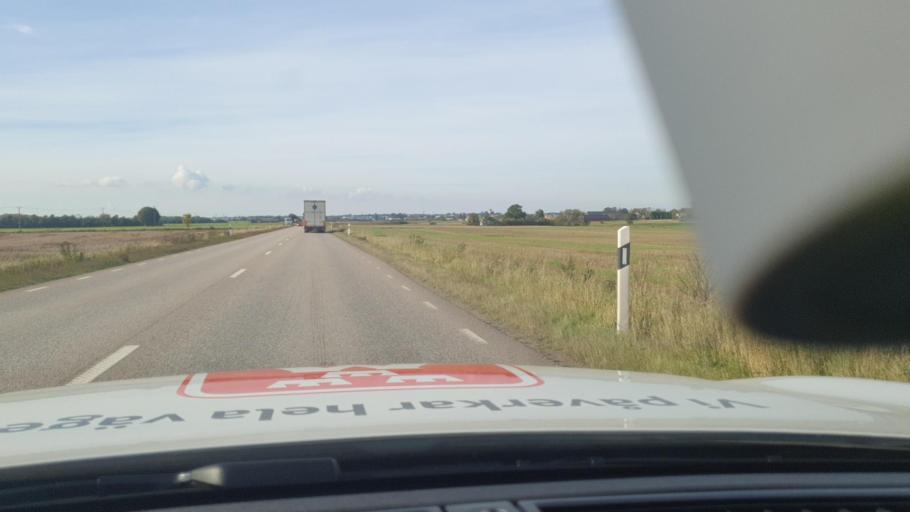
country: SE
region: Skane
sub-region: Angelholms Kommun
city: Munka-Ljungby
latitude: 56.2541
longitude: 12.9467
